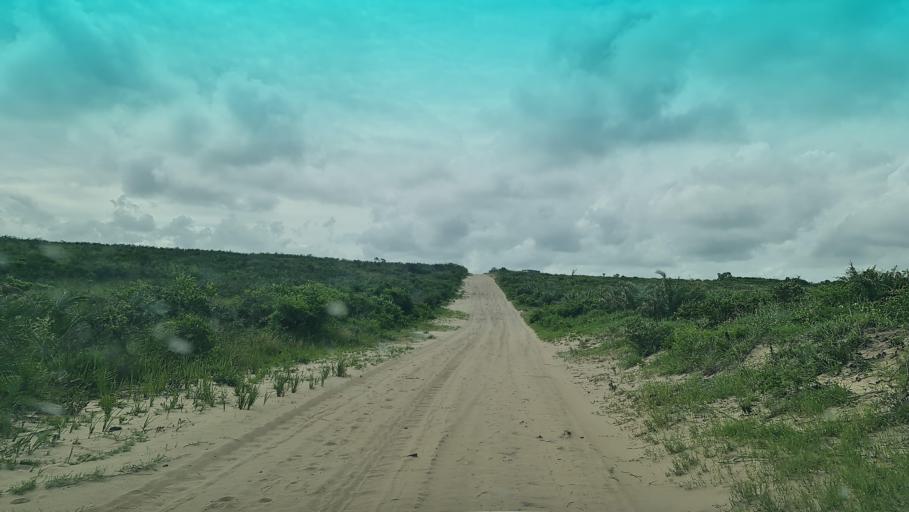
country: MZ
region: Maputo
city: Manhica
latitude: -25.4486
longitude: 32.9526
